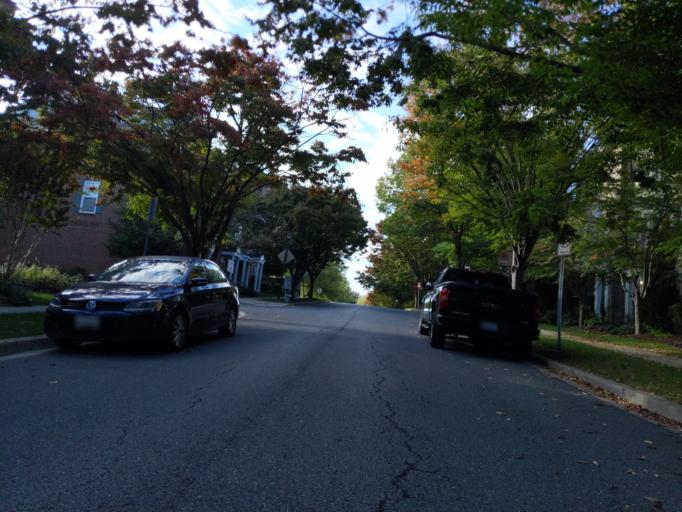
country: US
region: Maryland
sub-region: Montgomery County
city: Forest Glen
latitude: 39.0174
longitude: -77.0477
